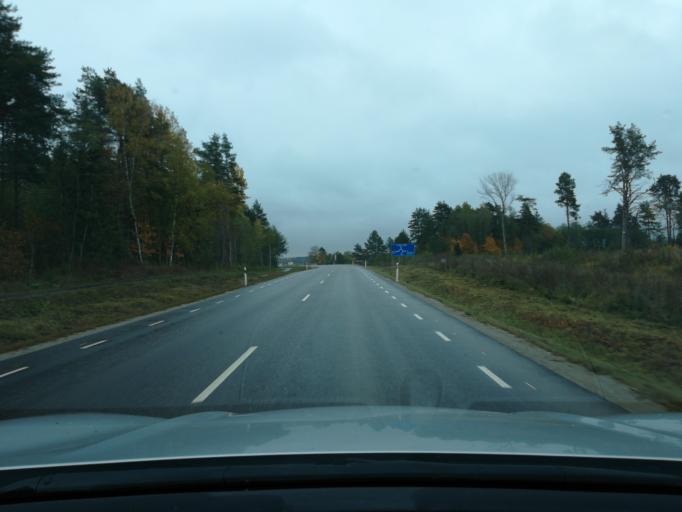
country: EE
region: Ida-Virumaa
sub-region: Johvi vald
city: Johvi
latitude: 59.2957
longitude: 27.4885
